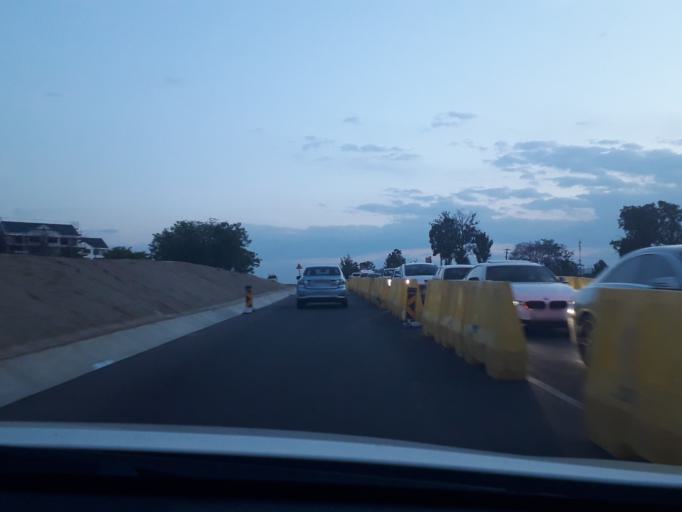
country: ZA
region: Gauteng
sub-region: City of Johannesburg Metropolitan Municipality
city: Midrand
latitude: -25.9839
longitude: 28.0765
